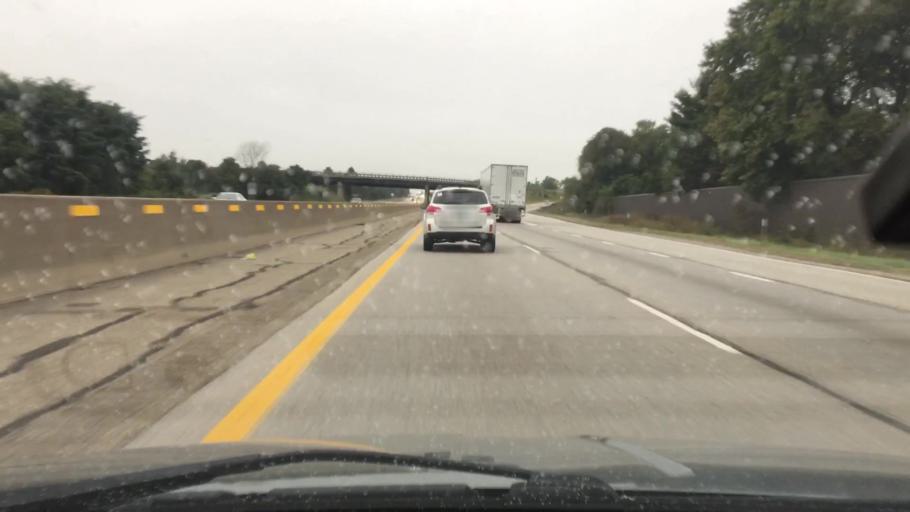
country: US
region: Michigan
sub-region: Kalamazoo County
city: Portage
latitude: 42.2476
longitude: -85.5530
